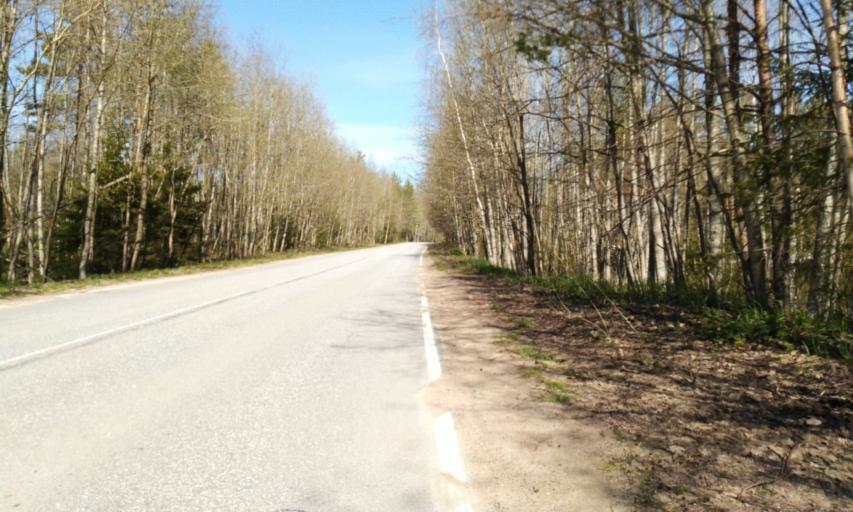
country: RU
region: Leningrad
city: Garbolovo
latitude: 60.4078
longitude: 30.4634
